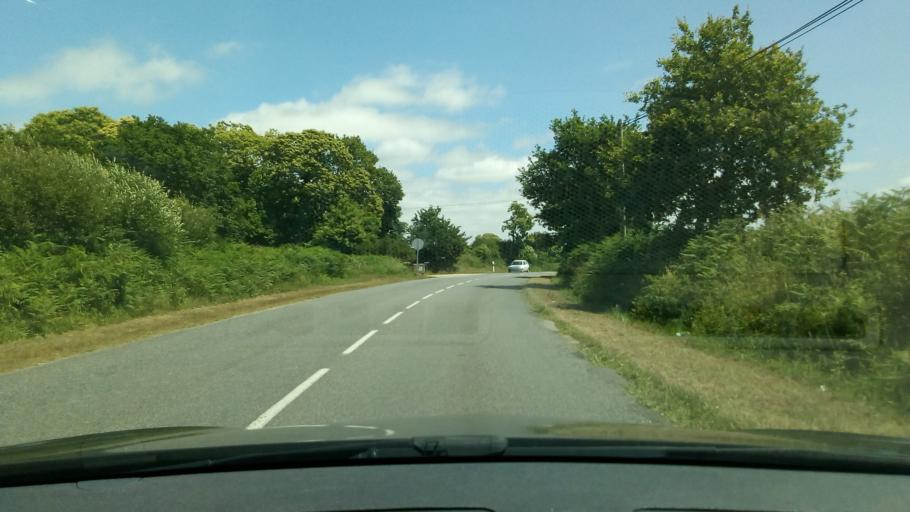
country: FR
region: Brittany
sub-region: Departement du Finistere
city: Melgven
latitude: 47.8864
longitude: -3.8153
